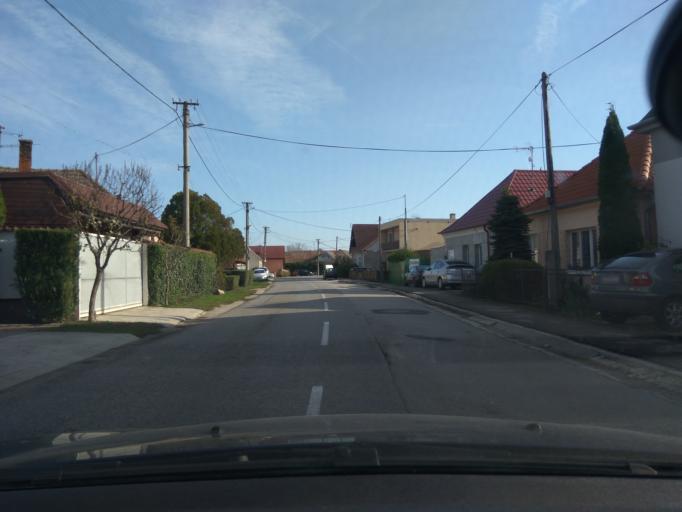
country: SK
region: Trnavsky
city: Vrbove
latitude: 48.6290
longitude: 17.7712
